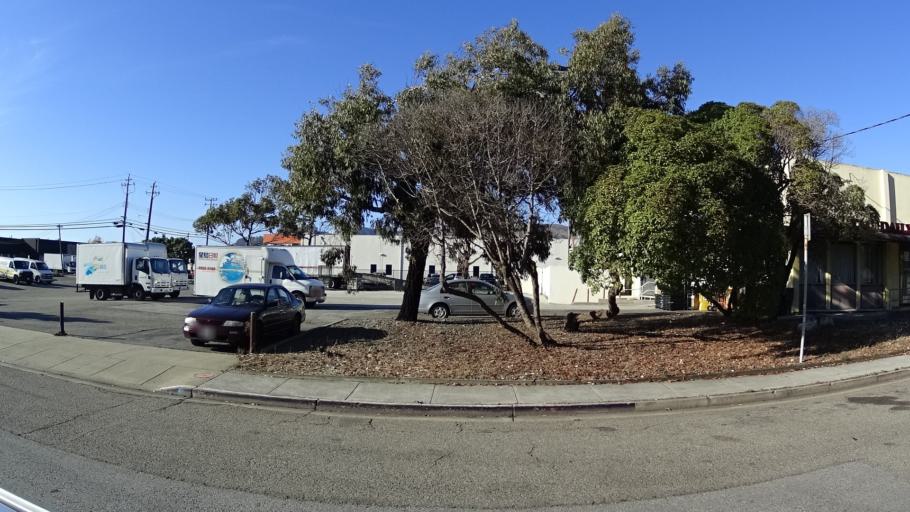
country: US
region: California
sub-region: San Mateo County
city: South San Francisco
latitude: 37.6442
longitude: -122.3980
